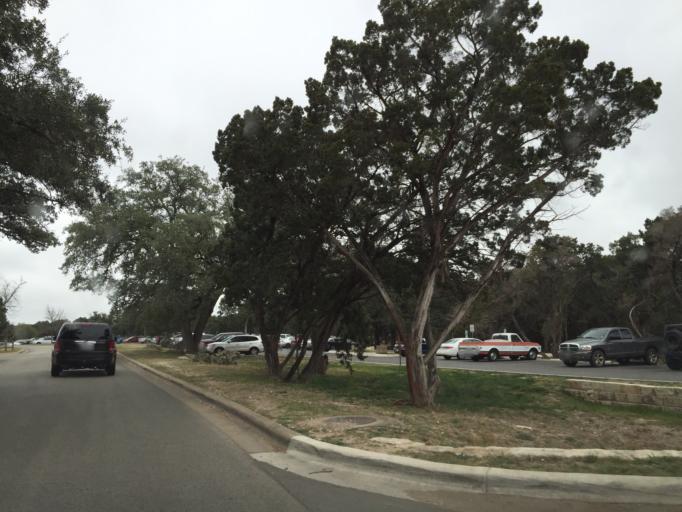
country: US
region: Texas
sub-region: Travis County
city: Wells Branch
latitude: 30.4018
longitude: -97.6848
